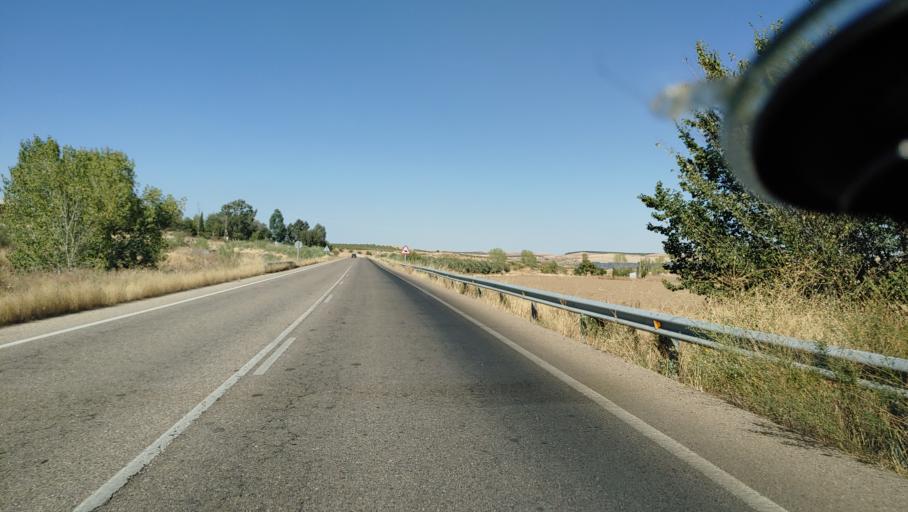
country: ES
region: Castille-La Mancha
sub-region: Province of Toledo
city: Casasbuenas
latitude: 39.7287
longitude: -4.1112
